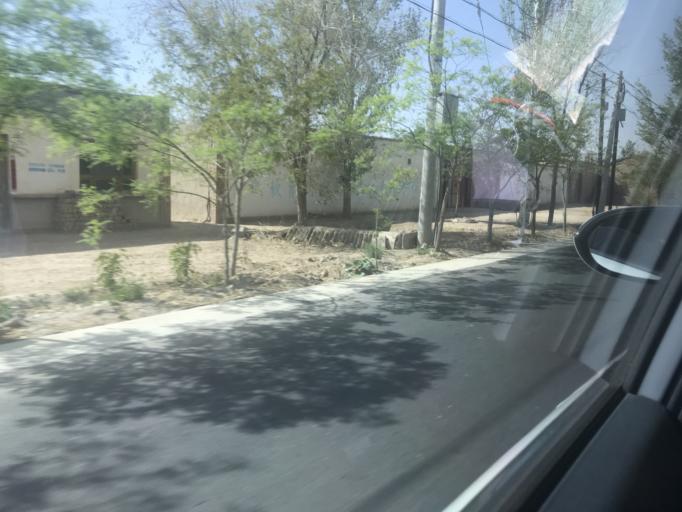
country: CN
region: Gansu Sheng
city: Gulang
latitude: 37.6571
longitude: 103.0993
